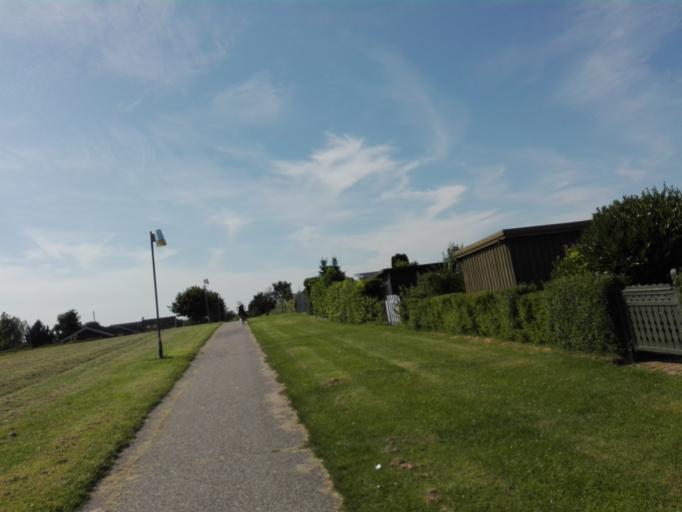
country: DK
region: Central Jutland
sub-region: Arhus Kommune
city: Marslet
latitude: 56.0893
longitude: 10.1495
